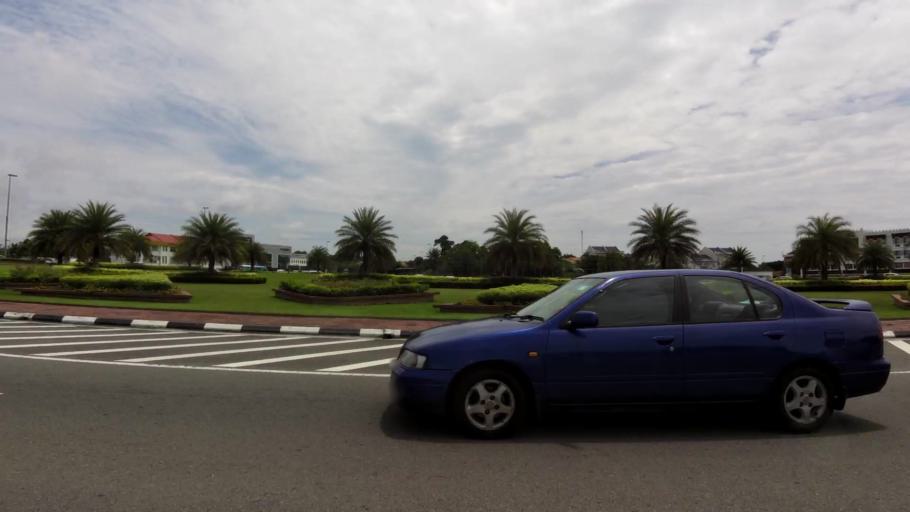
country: BN
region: Brunei and Muara
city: Bandar Seri Begawan
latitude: 4.9008
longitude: 114.9200
